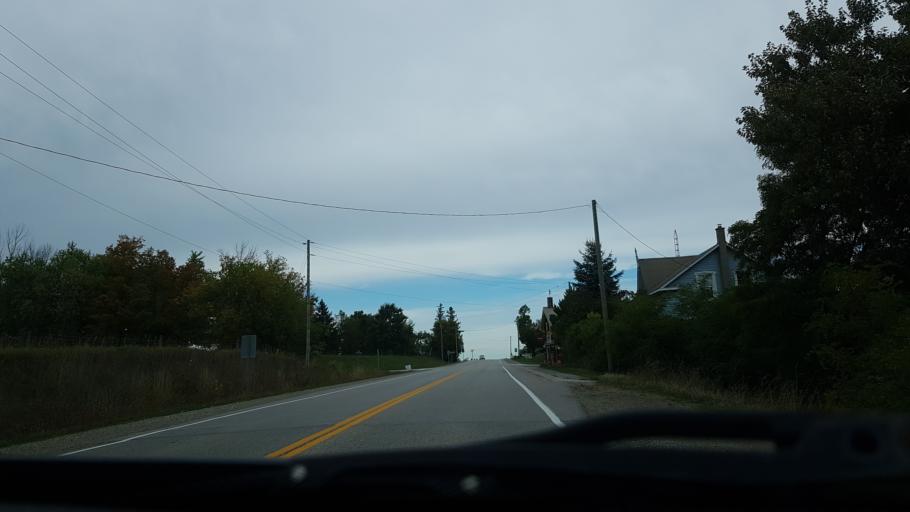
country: CA
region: Ontario
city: Shelburne
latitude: 44.1416
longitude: -80.0315
